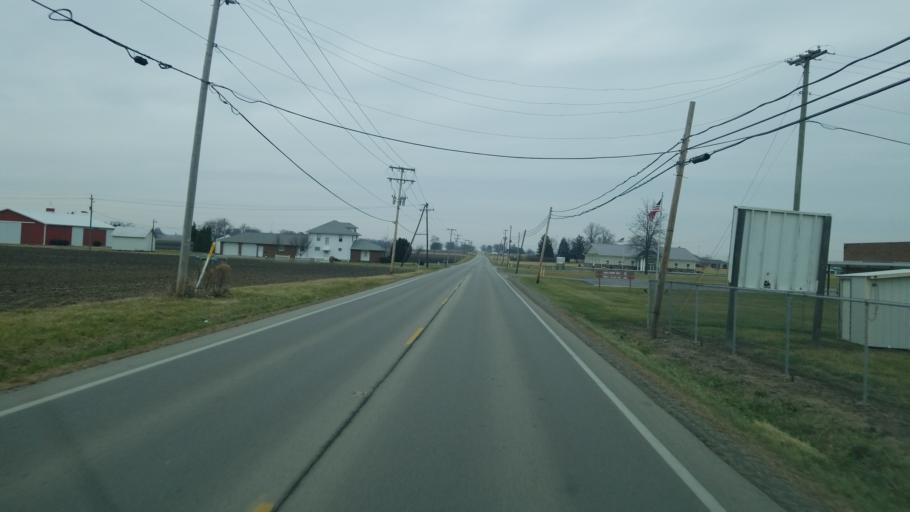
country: US
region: Ohio
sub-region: Wyandot County
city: Upper Sandusky
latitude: 40.8483
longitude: -83.2801
